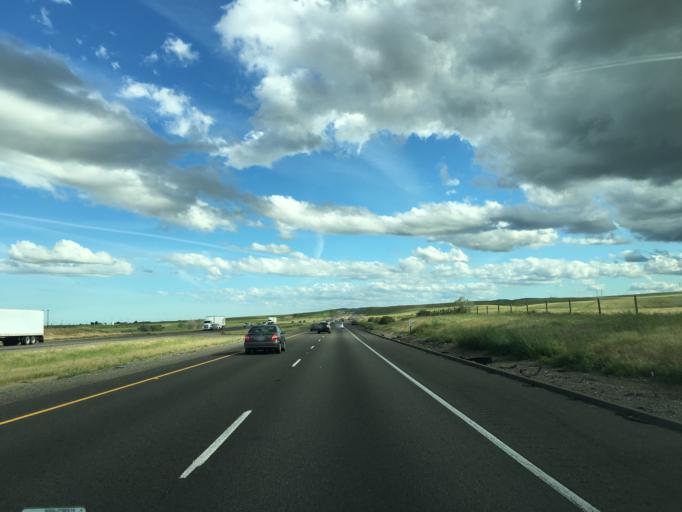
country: US
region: California
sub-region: Merced County
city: Los Banos
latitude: 37.0047
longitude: -120.9197
